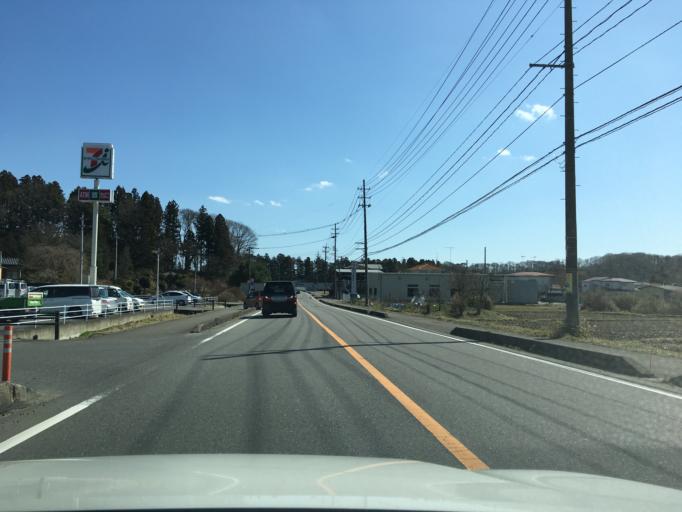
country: JP
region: Tochigi
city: Kuroiso
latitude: 37.1043
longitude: 140.1689
